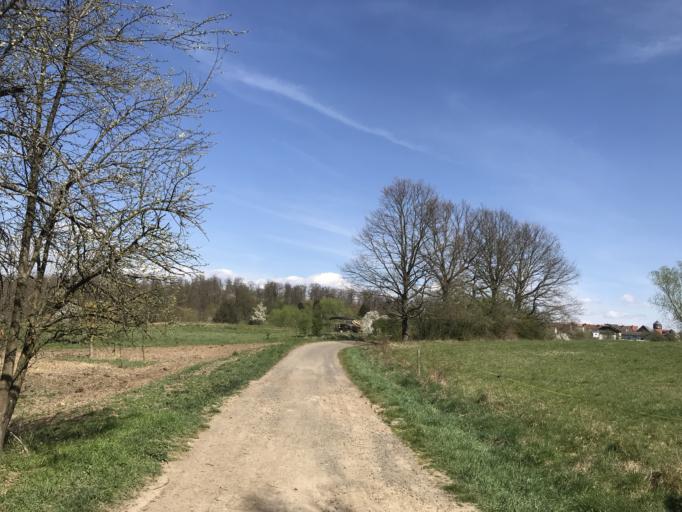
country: DE
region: Hesse
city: Beuern
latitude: 50.6561
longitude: 8.8091
